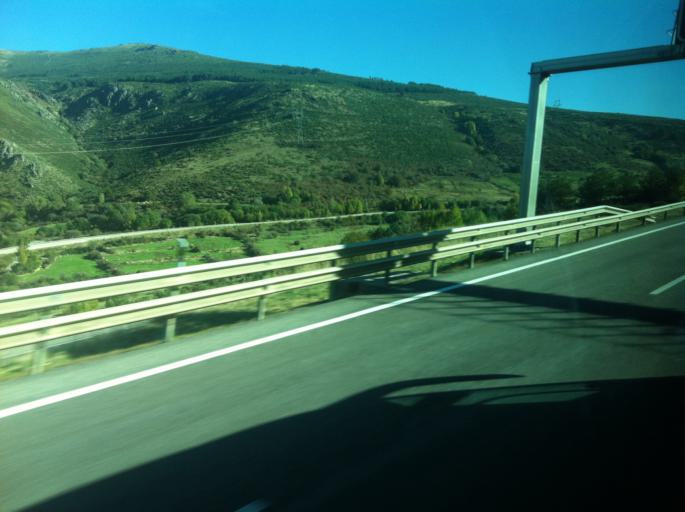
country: ES
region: Madrid
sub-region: Provincia de Madrid
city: Somosierra
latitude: 41.1459
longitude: -3.5833
